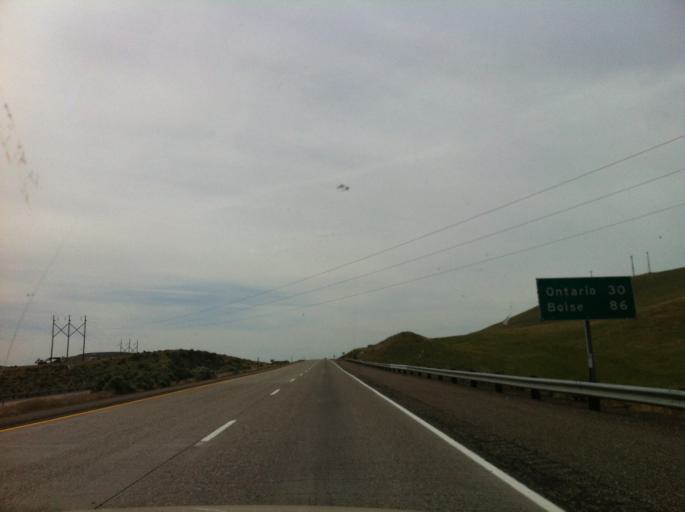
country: US
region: Idaho
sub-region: Washington County
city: Weiser
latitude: 44.3632
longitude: -117.2936
